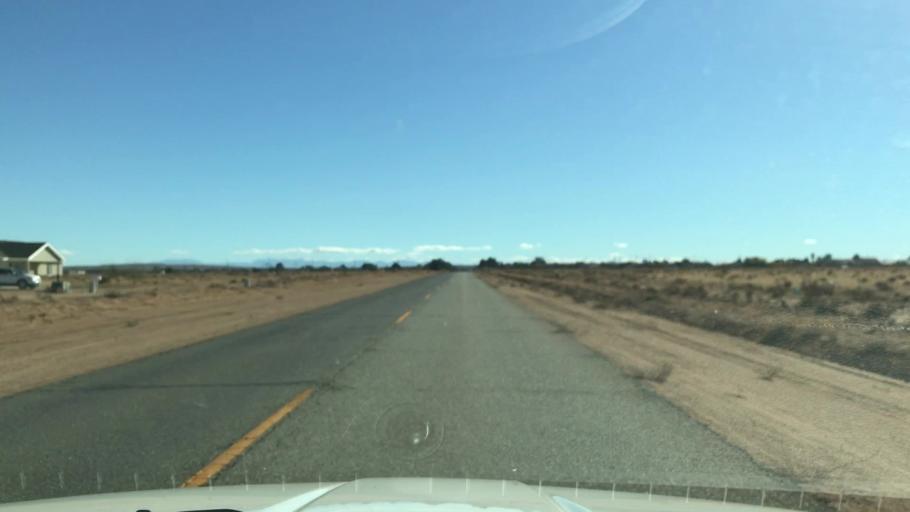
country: US
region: California
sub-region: Kern County
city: California City
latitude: 35.1394
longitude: -117.9859
